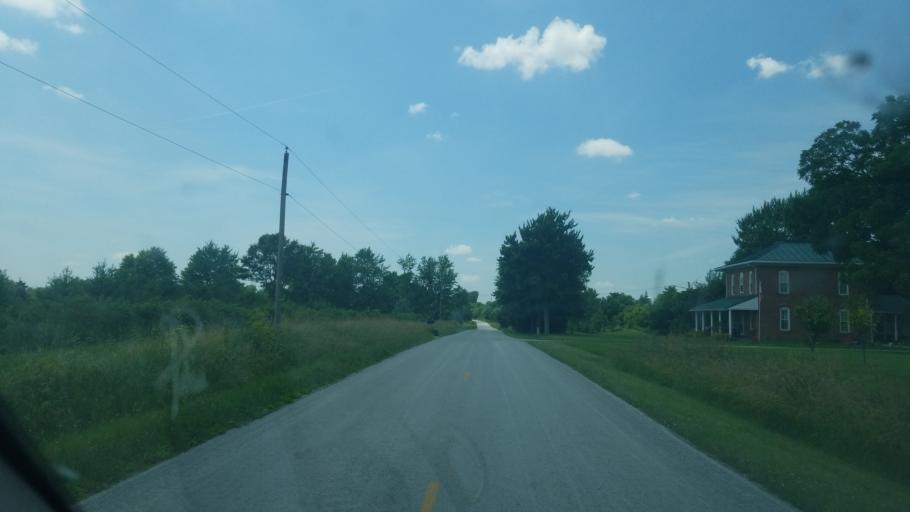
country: US
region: Ohio
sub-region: Hancock County
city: Arlington
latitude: 40.7899
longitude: -83.6255
